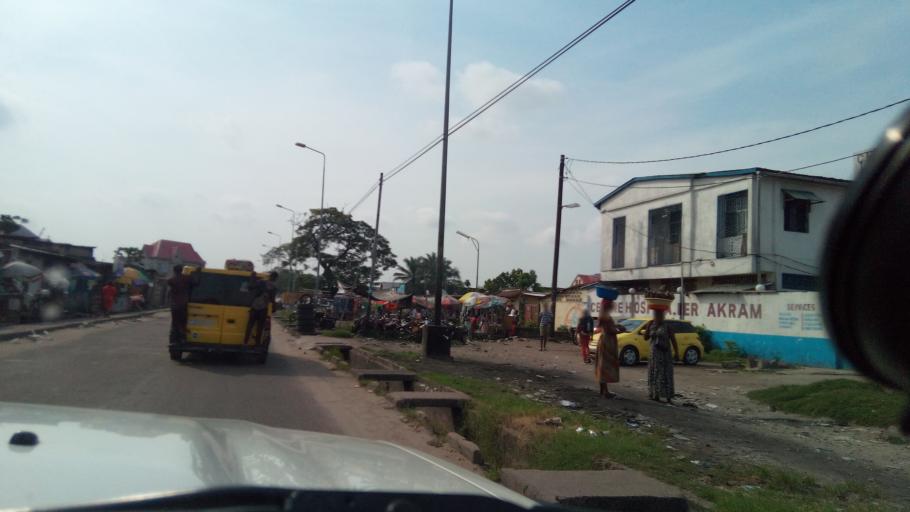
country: CD
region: Kinshasa
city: Kinshasa
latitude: -4.3495
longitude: 15.3203
